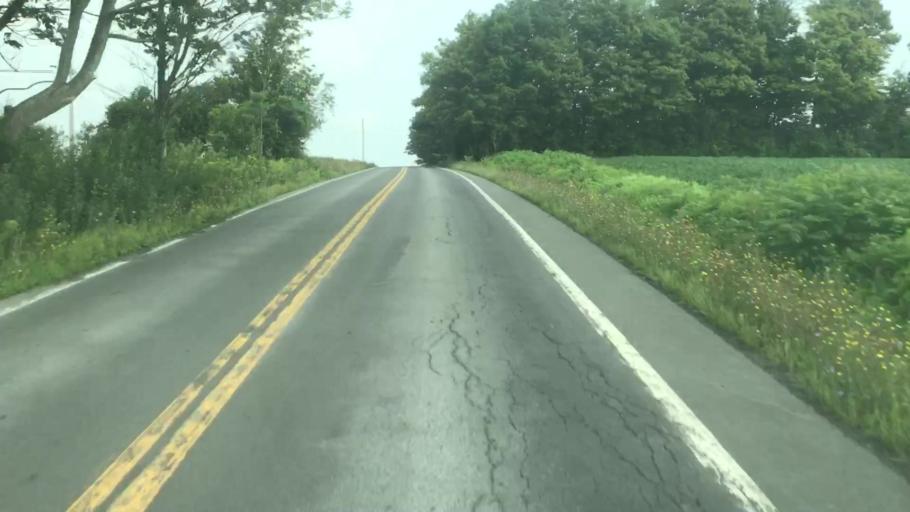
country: US
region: New York
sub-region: Onondaga County
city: Skaneateles
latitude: 42.8902
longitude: -76.4499
